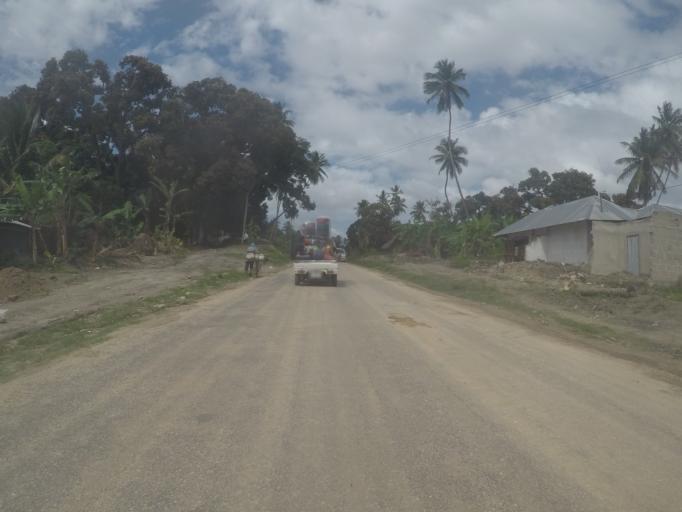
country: TZ
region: Zanzibar North
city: Mkokotoni
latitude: -5.8753
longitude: 39.2608
